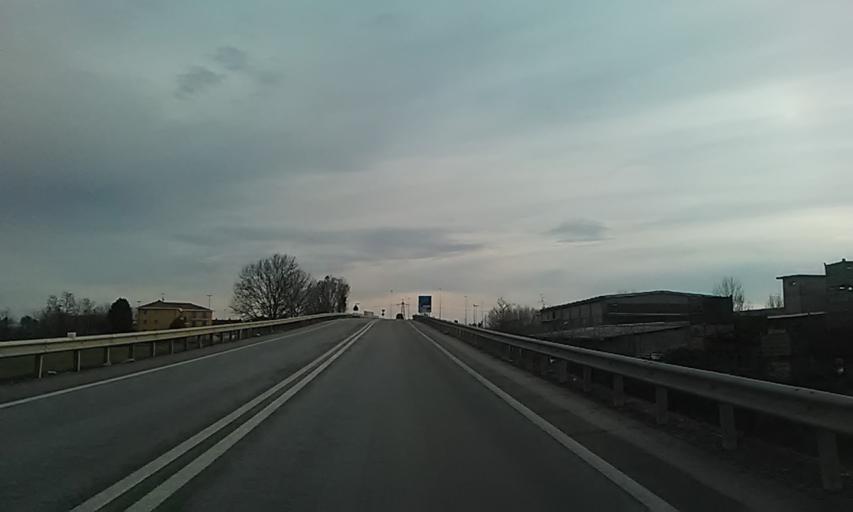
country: IT
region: Piedmont
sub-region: Provincia di Torino
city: Rondissone
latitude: 45.2440
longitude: 7.9581
